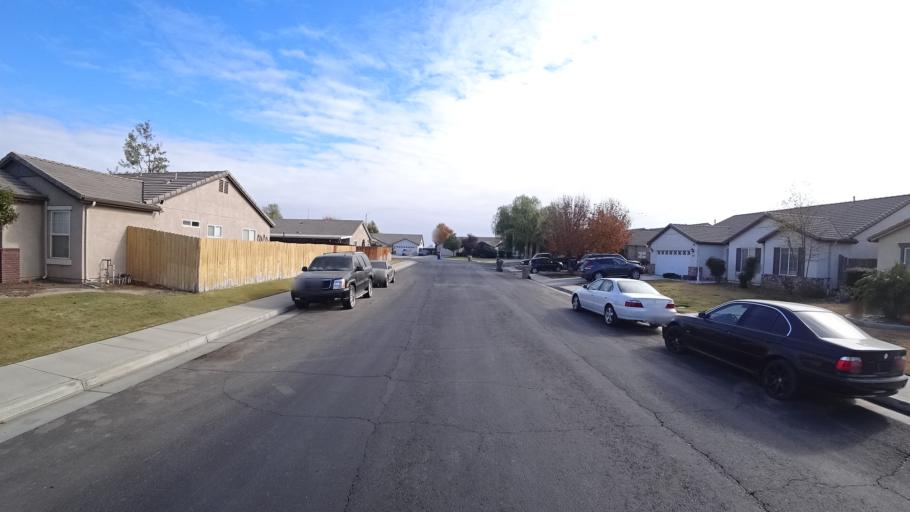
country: US
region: California
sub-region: Kern County
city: Greenacres
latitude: 35.2968
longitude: -119.1202
